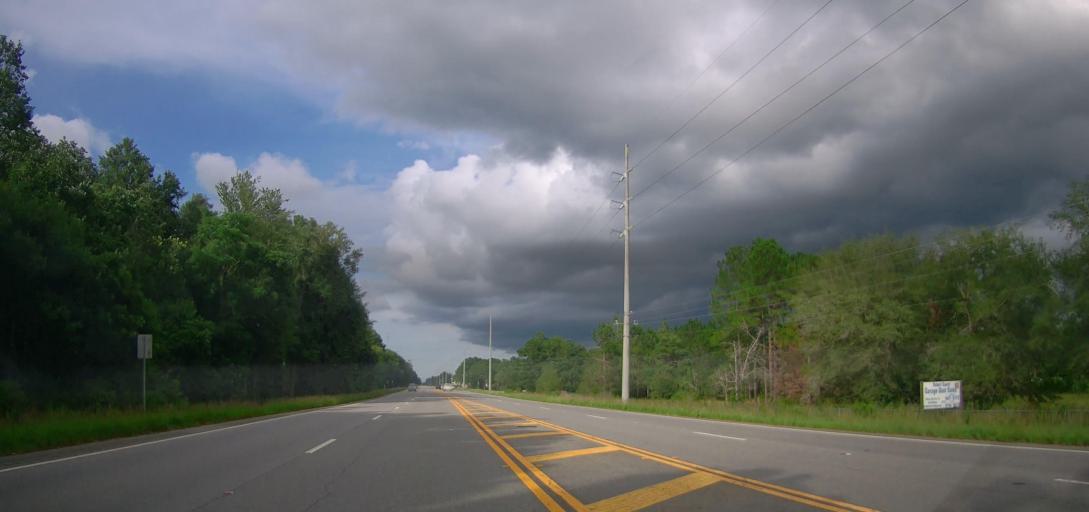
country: US
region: Georgia
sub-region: Pierce County
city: Blackshear
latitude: 31.3957
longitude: -82.1298
